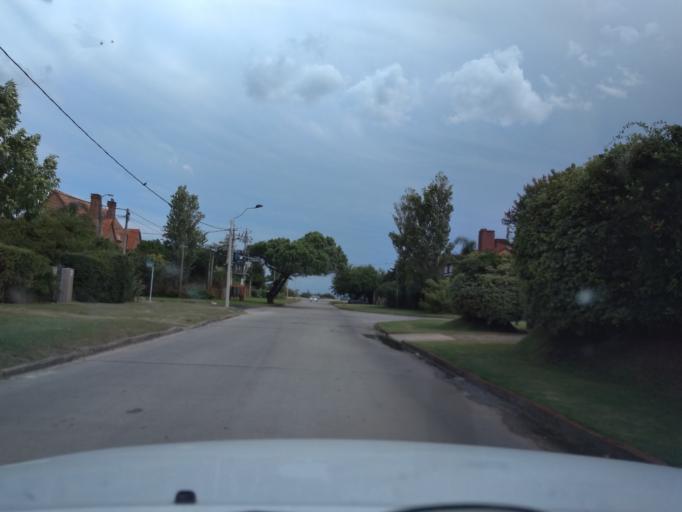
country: UY
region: Canelones
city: Barra de Carrasco
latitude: -34.8859
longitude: -56.0477
